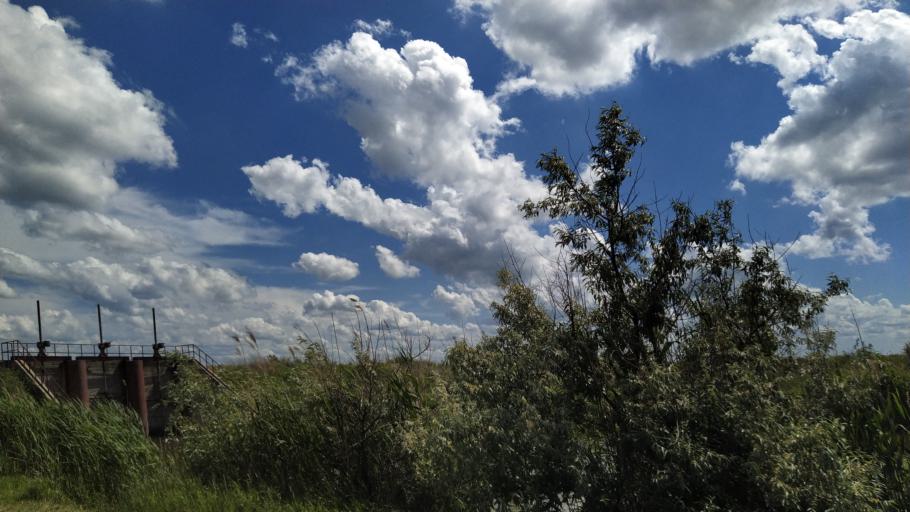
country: RU
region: Rostov
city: Bataysk
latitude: 47.1331
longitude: 39.6784
